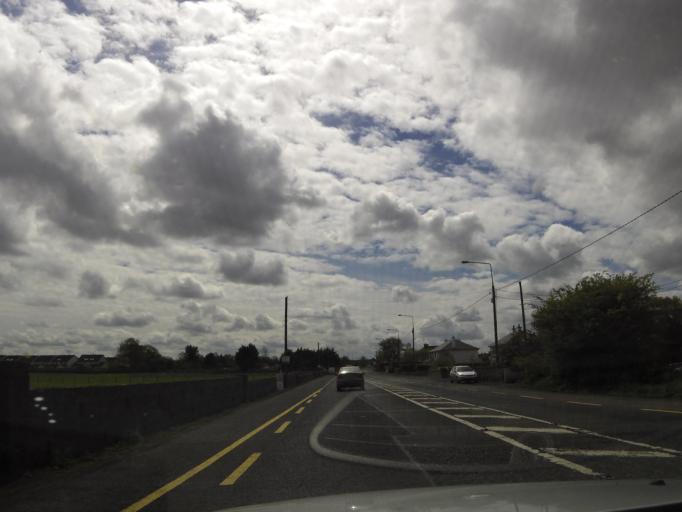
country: IE
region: Connaught
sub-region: County Galway
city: Tuam
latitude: 53.5284
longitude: -8.8493
